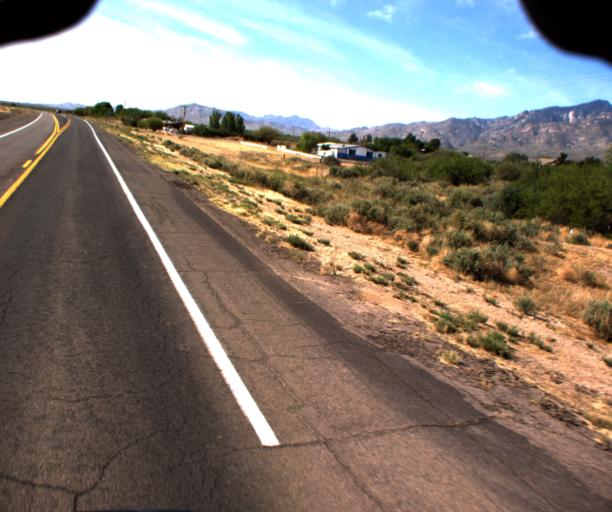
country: US
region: Arizona
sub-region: Graham County
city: Swift Trail Junction
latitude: 32.6892
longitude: -109.7077
